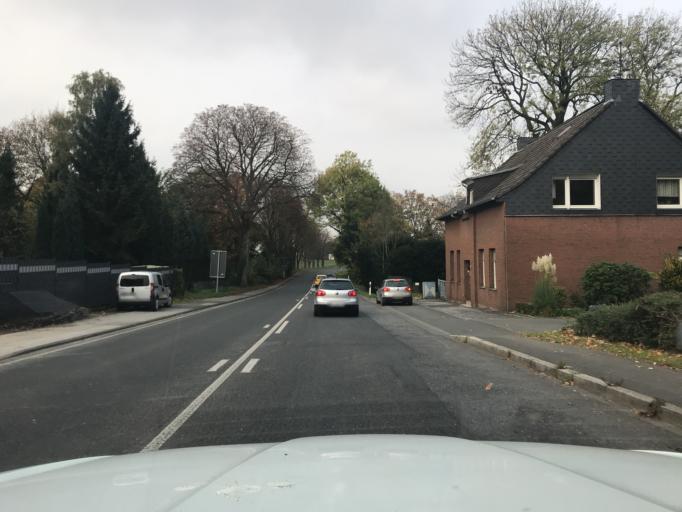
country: DE
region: North Rhine-Westphalia
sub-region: Regierungsbezirk Dusseldorf
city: Velbert
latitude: 51.3540
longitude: 7.0215
